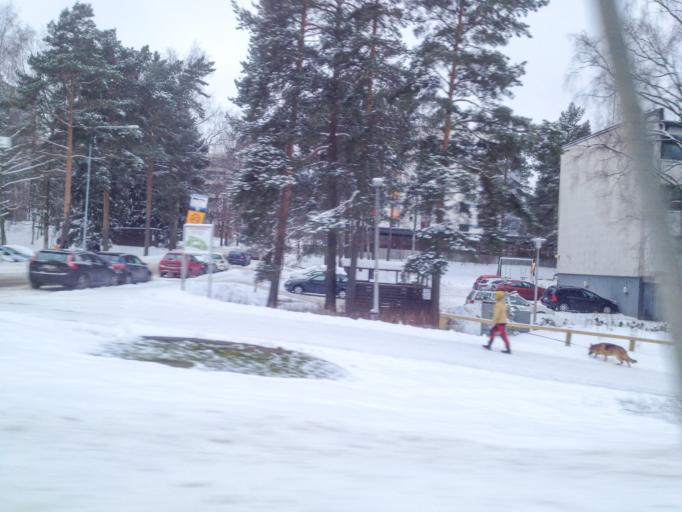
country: FI
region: Uusimaa
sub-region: Helsinki
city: Vantaa
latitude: 60.2180
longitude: 25.1329
